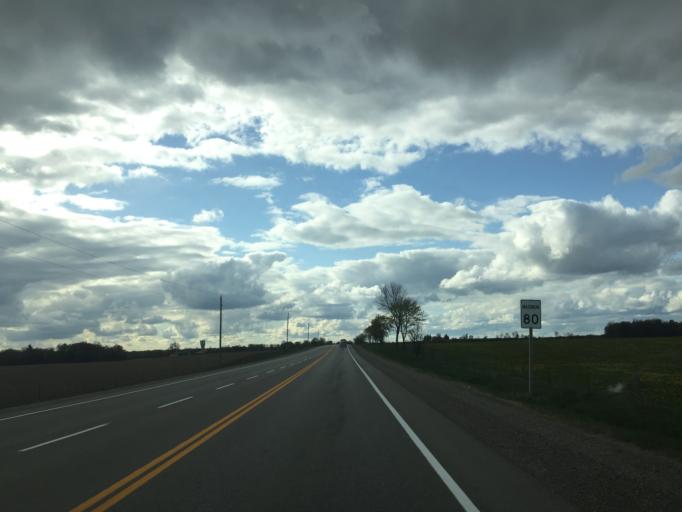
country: CA
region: Ontario
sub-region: Wellington County
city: Guelph
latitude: 43.5083
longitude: -80.3091
